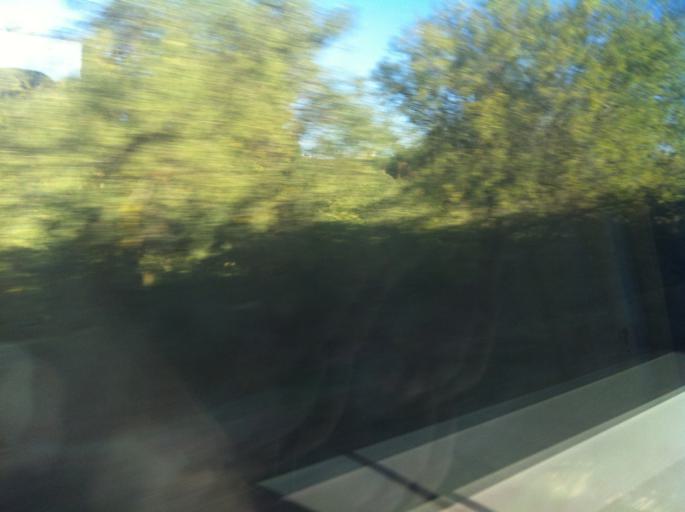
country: ES
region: Castille and Leon
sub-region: Provincia de Palencia
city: Soto de Cerrato
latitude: 41.9531
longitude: -4.4523
